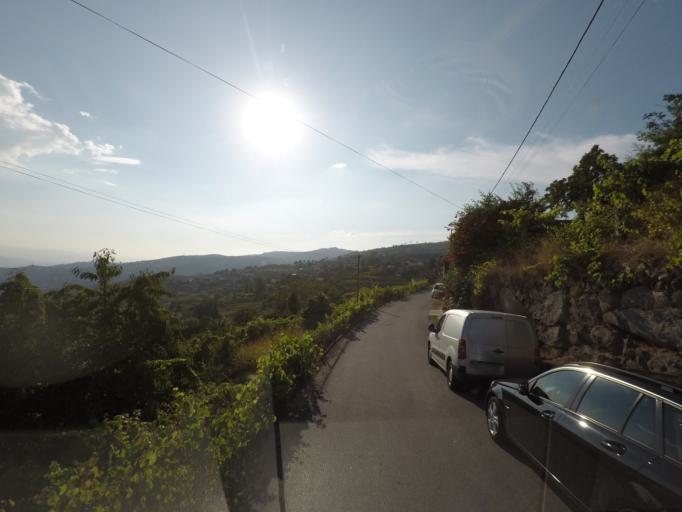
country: PT
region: Vila Real
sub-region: Mesao Frio
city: Mesao Frio
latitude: 41.1659
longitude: -7.9241
